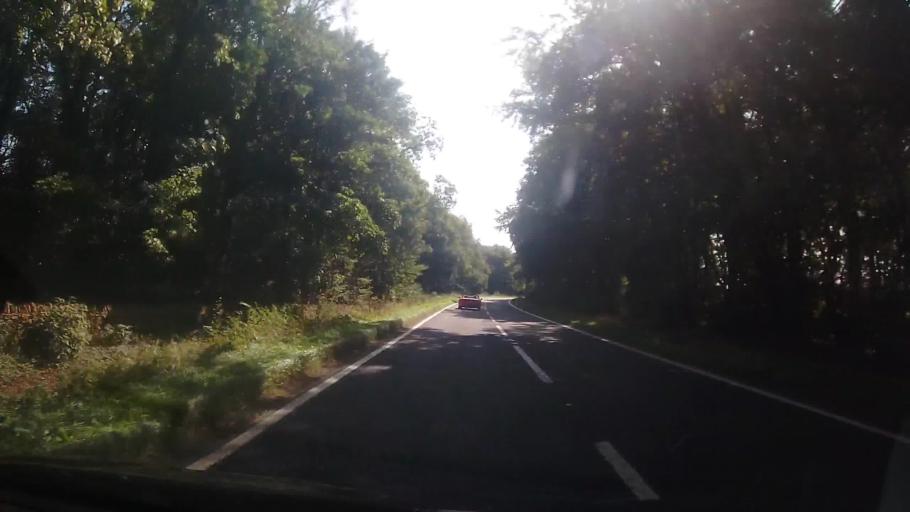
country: GB
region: England
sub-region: Gloucestershire
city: Chipping Campden
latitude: 52.0061
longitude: -1.7903
